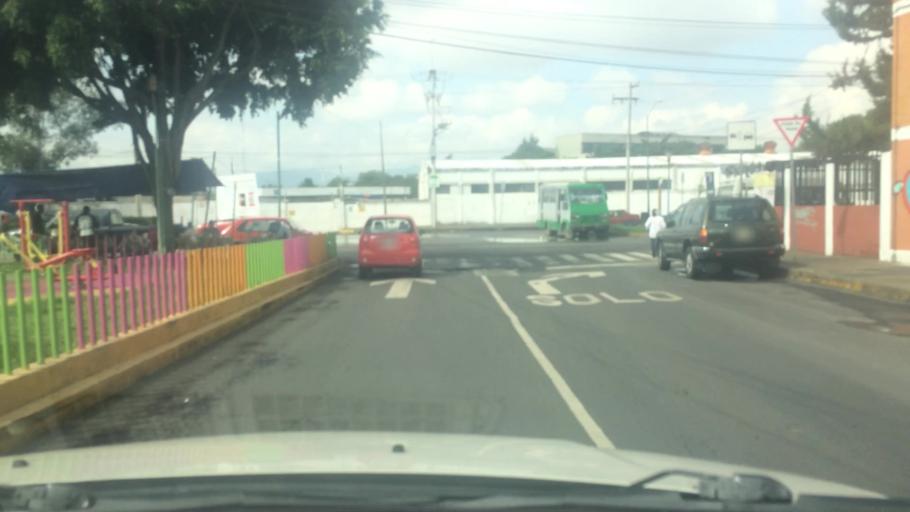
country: MX
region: Mexico City
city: Xochimilco
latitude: 19.3072
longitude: -99.1006
